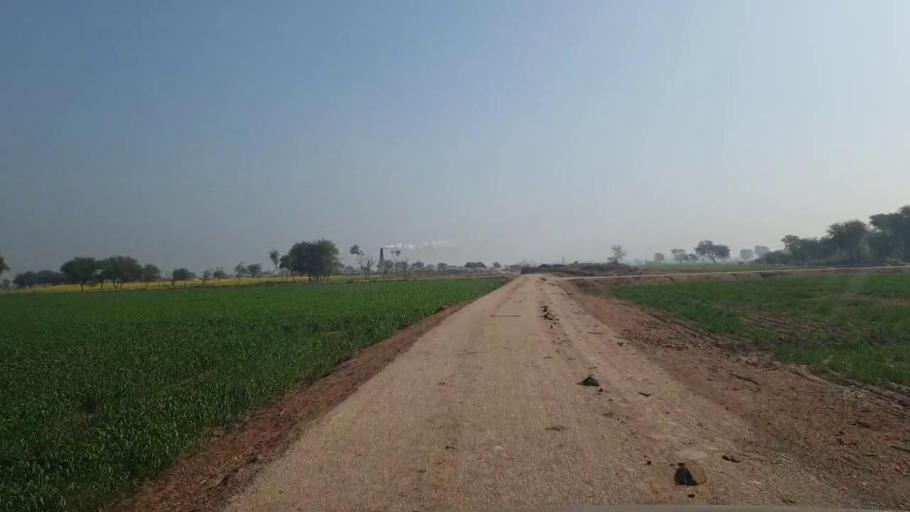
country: PK
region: Sindh
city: Shahdadpur
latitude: 25.9646
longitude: 68.5858
